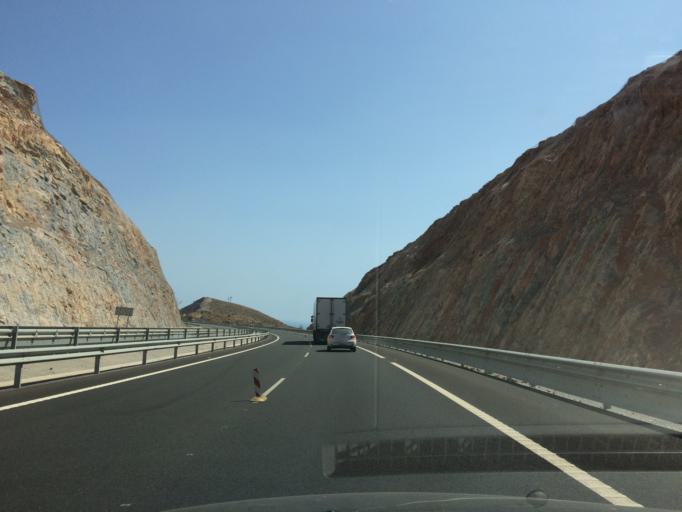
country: ES
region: Andalusia
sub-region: Provincia de Granada
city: Gualchos
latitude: 36.7124
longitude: -3.4216
